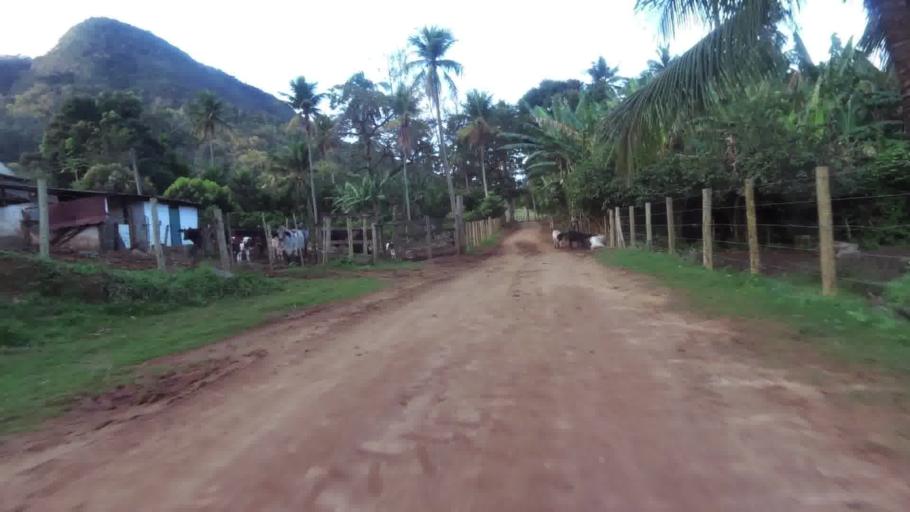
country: BR
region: Espirito Santo
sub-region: Guarapari
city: Guarapari
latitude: -20.6812
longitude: -40.6286
